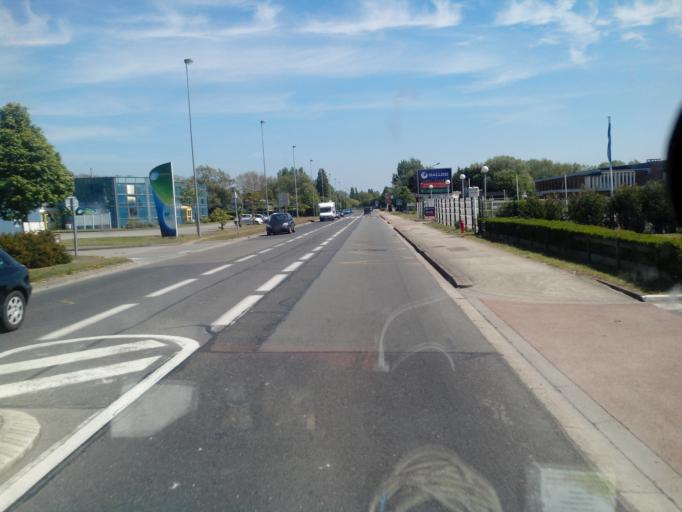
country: FR
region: Nord-Pas-de-Calais
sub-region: Departement du Pas-de-Calais
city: Saint-Leonard
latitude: 50.6903
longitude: 1.6164
